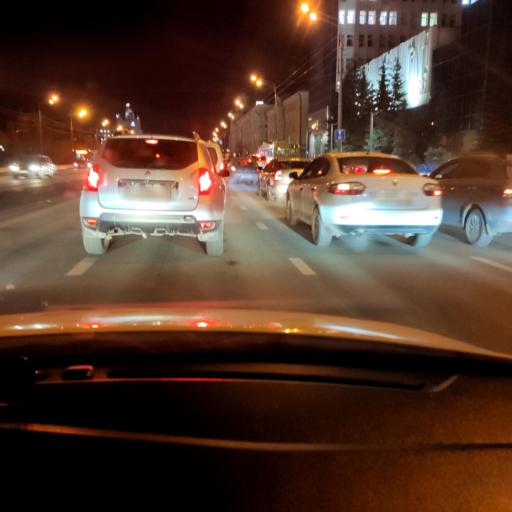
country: RU
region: Tatarstan
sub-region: Gorod Kazan'
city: Kazan
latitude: 55.7937
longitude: 49.1589
